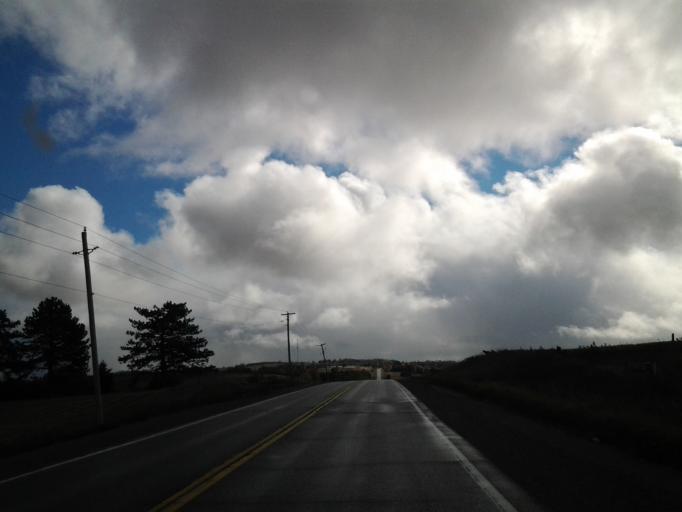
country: CA
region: Ontario
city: Shelburne
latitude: 44.1342
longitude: -80.0297
